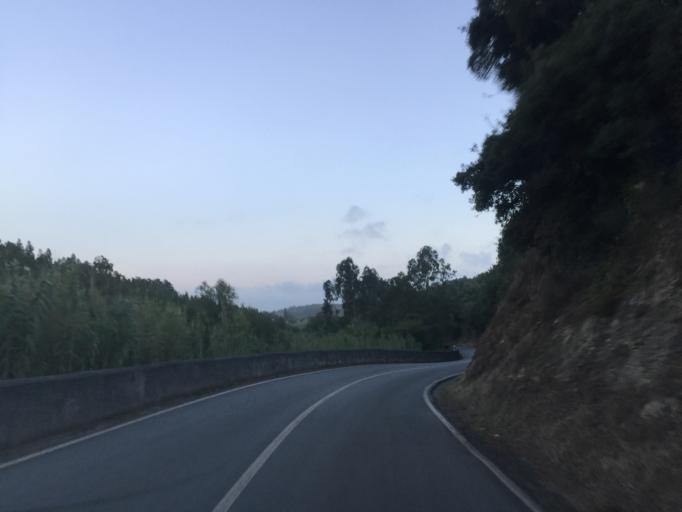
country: PT
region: Leiria
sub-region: Bombarral
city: Bombarral
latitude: 39.2962
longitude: -9.2003
